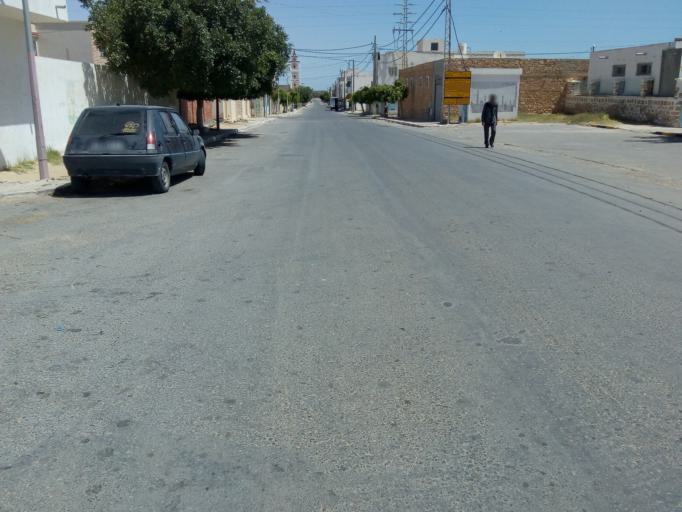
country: TN
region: Qabis
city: Gabes
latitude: 33.9574
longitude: 10.0127
